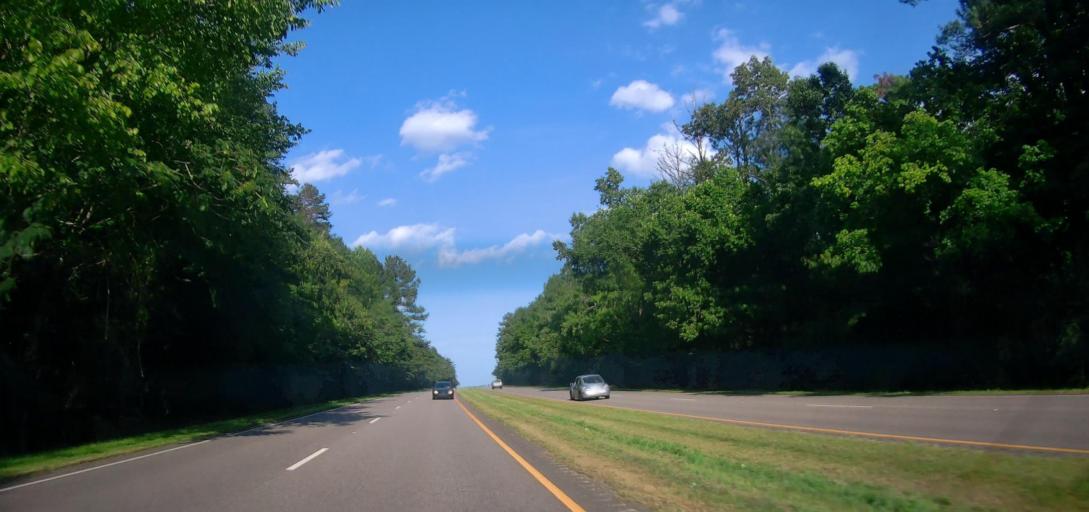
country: US
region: Alabama
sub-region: Jefferson County
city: Leeds
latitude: 33.5457
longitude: -86.6099
